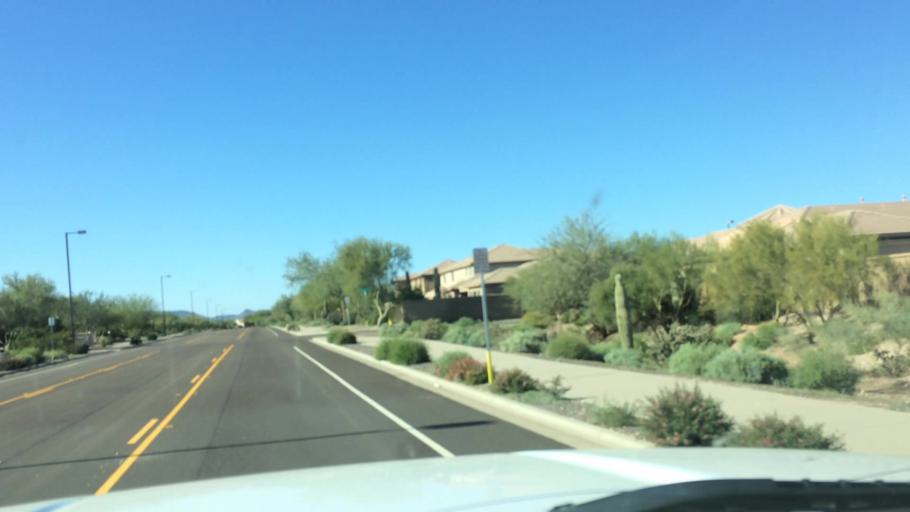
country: US
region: Arizona
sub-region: Maricopa County
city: Anthem
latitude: 33.8480
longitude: -112.1046
